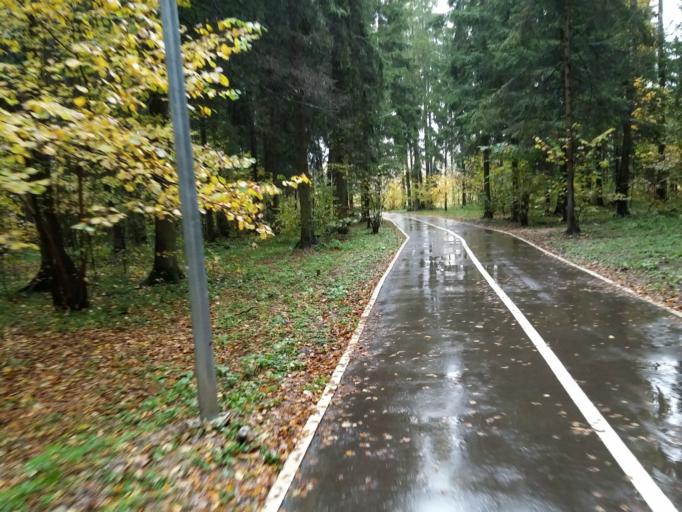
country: RU
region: Moskovskaya
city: Selyatino
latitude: 55.5166
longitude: 36.9894
